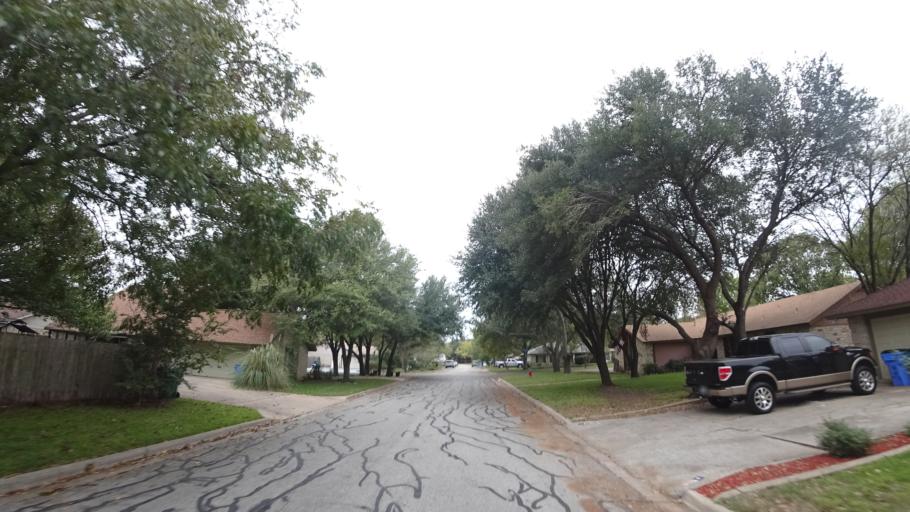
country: US
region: Texas
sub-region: Travis County
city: Pflugerville
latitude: 30.4496
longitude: -97.6206
